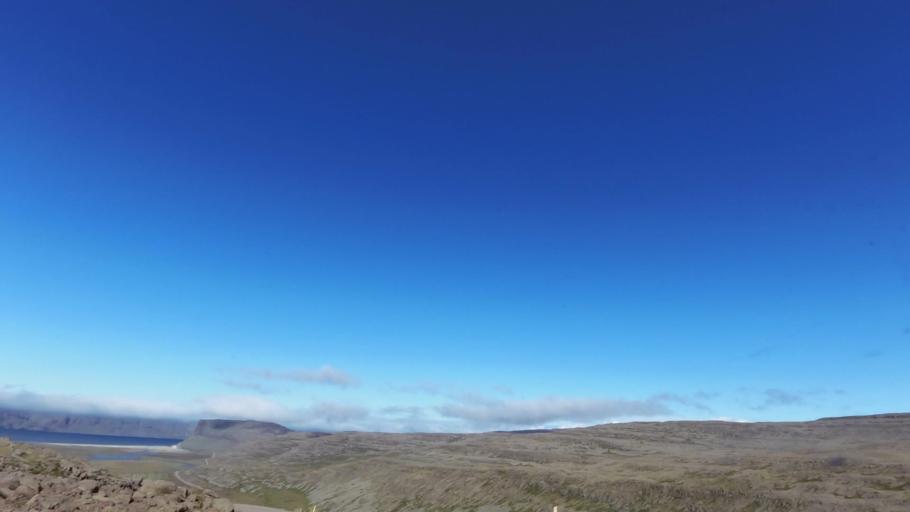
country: IS
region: West
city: Olafsvik
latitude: 65.5501
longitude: -24.2078
